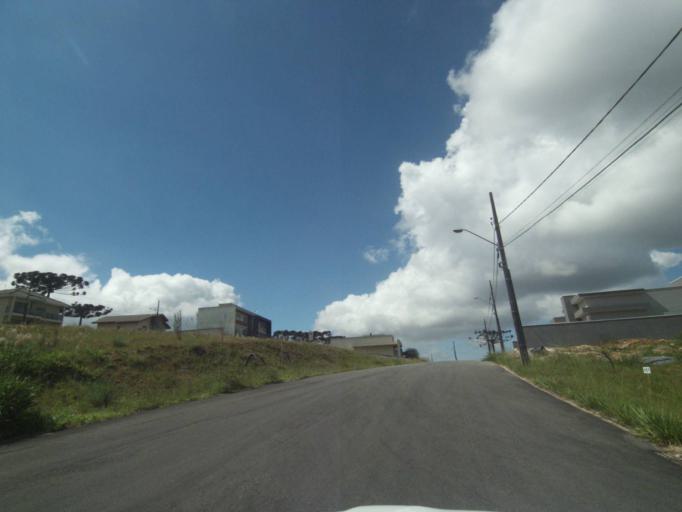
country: BR
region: Parana
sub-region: Colombo
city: Colombo
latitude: -25.3115
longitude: -49.2333
